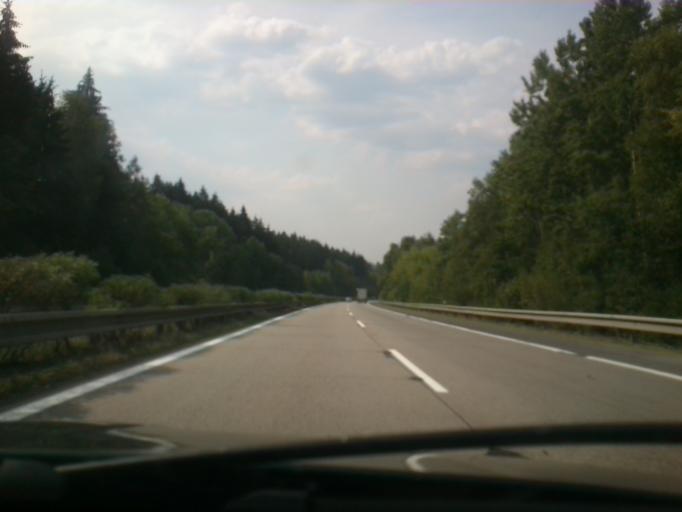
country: CZ
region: Central Bohemia
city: Divisov
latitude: 49.8103
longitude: 14.8860
